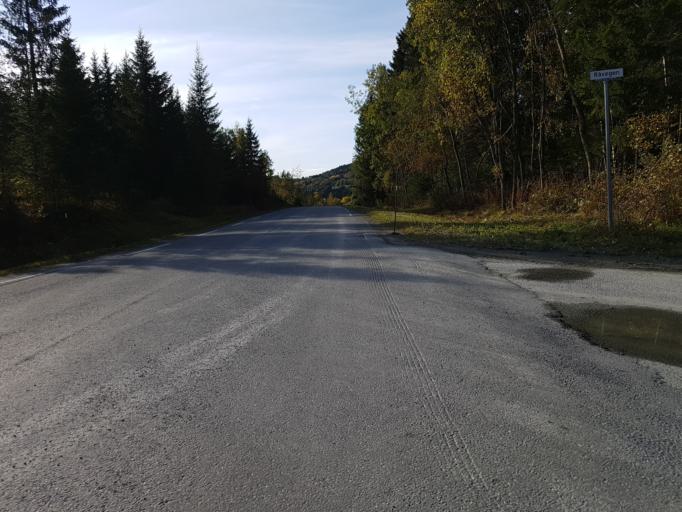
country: NO
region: Sor-Trondelag
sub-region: Klaebu
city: Klaebu
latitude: 63.3475
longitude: 10.5096
